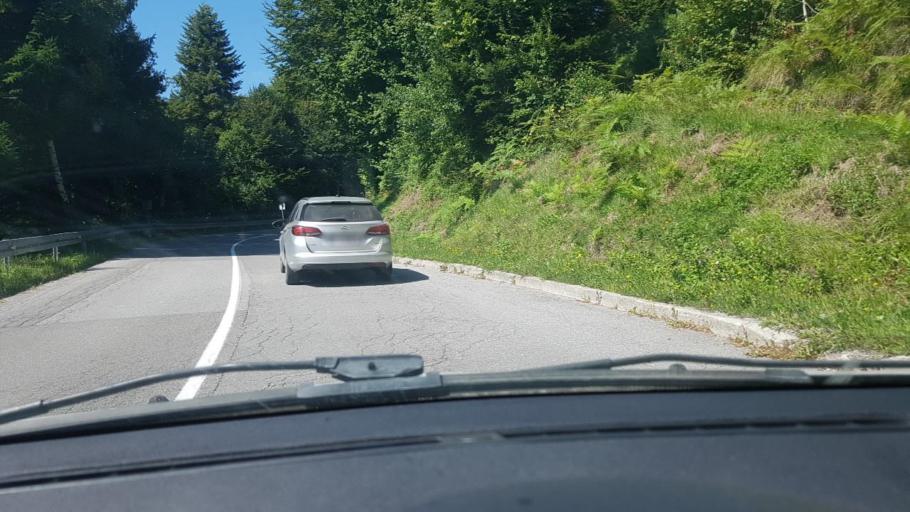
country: HR
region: Primorsko-Goranska
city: Vrbovsko
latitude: 45.3778
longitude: 14.9702
